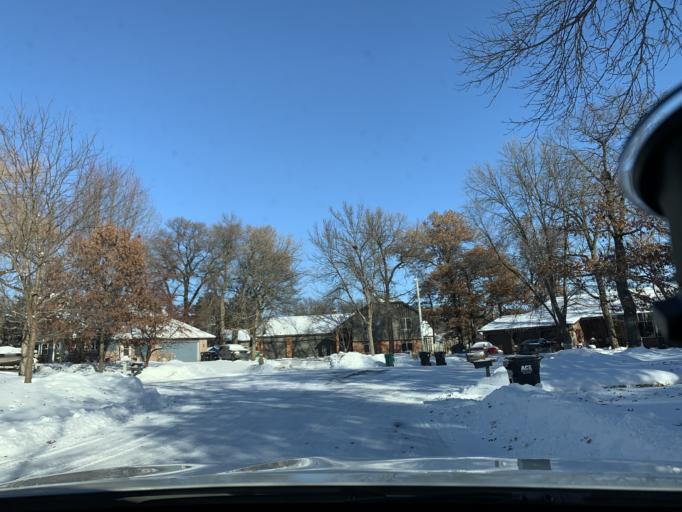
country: US
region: Minnesota
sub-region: Anoka County
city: Coon Rapids
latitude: 45.1673
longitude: -93.3002
